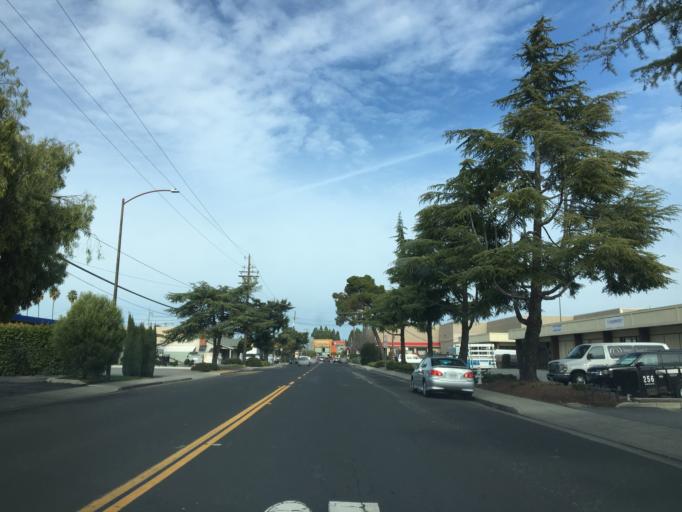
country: US
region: California
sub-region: Santa Clara County
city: Mountain View
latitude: 37.4197
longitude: -122.0969
